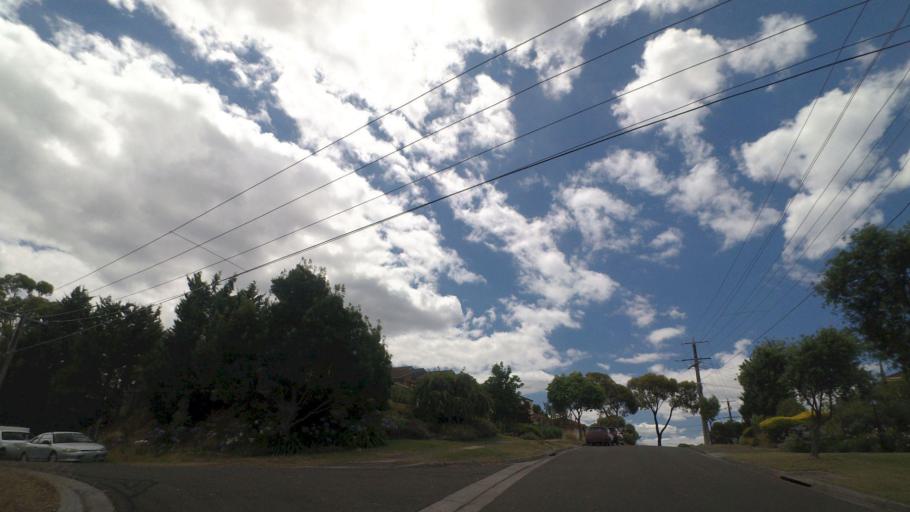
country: AU
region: Victoria
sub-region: Maroondah
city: Warranwood
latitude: -37.7757
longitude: 145.2406
